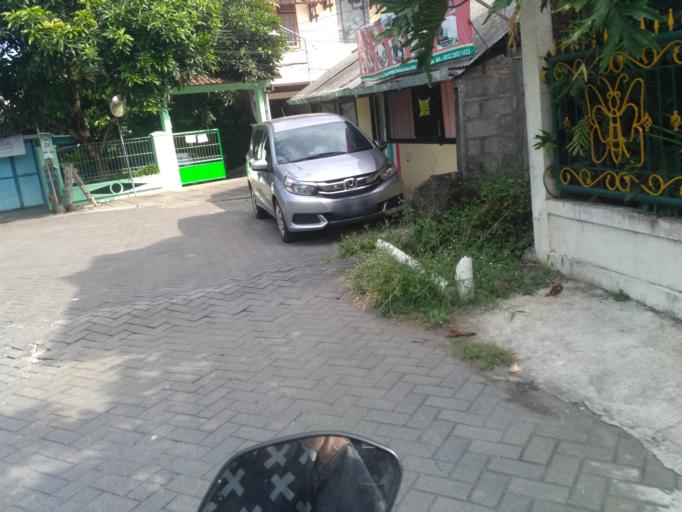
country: ID
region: Daerah Istimewa Yogyakarta
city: Depok
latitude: -7.7804
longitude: 110.4113
